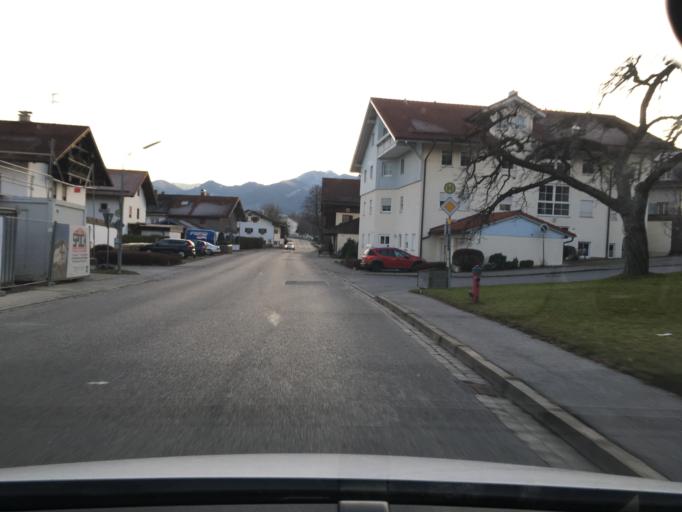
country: DE
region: Bavaria
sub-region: Upper Bavaria
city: Raubling
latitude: 47.7781
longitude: 12.1075
